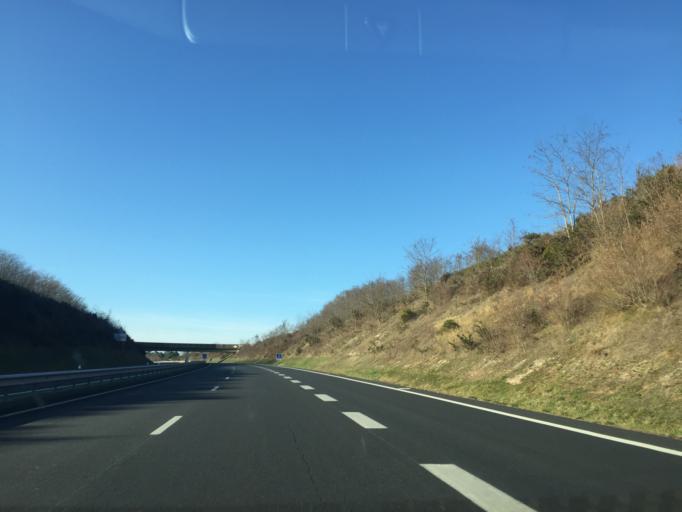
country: FR
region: Limousin
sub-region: Departement de la Correze
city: Cublac
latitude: 45.1709
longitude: 1.3218
